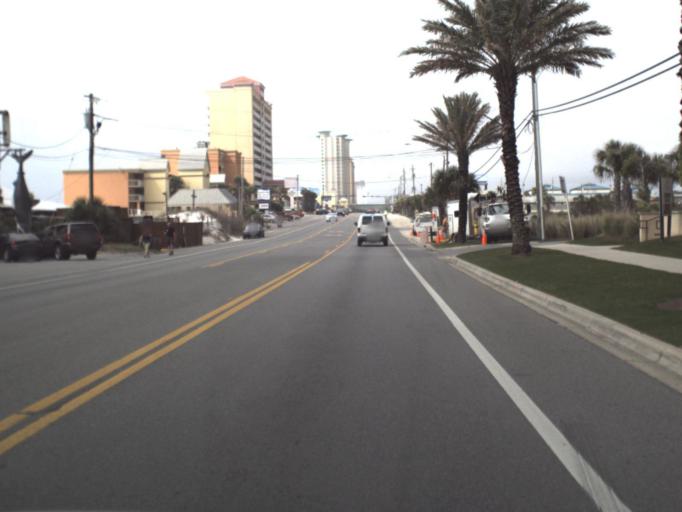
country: US
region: Florida
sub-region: Bay County
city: Panama City Beach
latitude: 30.2084
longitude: -85.8629
